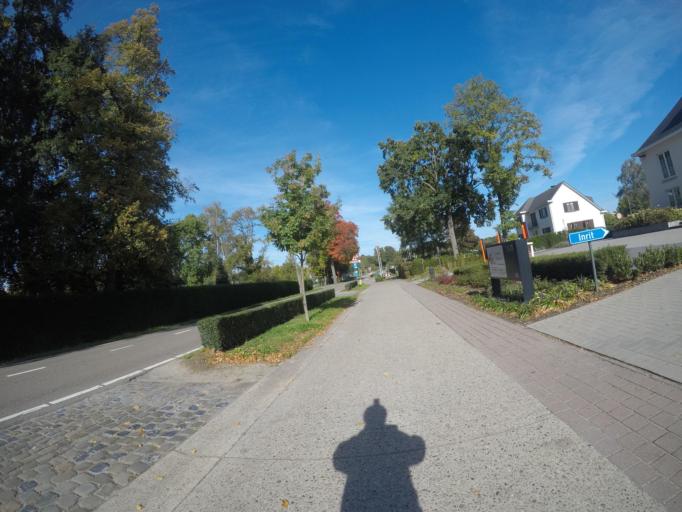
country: BE
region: Flanders
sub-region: Provincie Limburg
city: Diepenbeek
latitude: 50.9121
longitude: 5.4215
